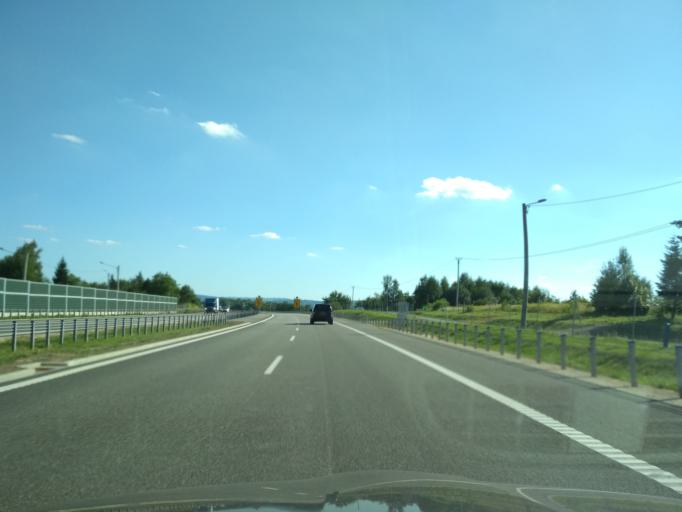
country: PL
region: Subcarpathian Voivodeship
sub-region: Powiat rzeszowski
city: Kielanowka
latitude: 50.0265
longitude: 21.9230
